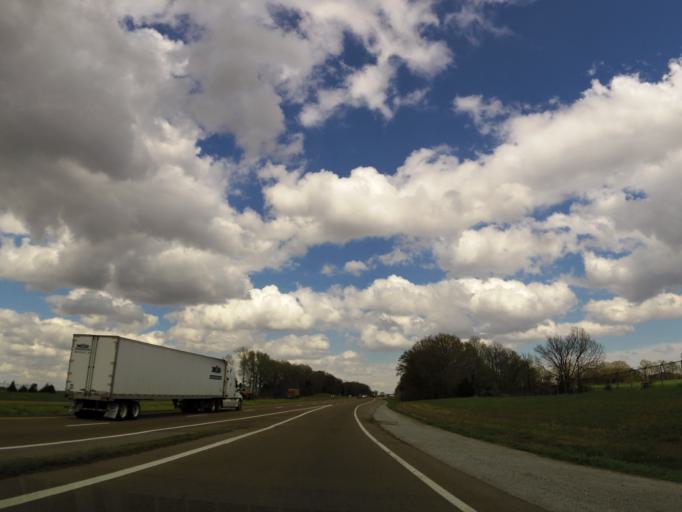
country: US
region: Tennessee
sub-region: Crockett County
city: Bells
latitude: 35.5973
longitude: -89.0533
